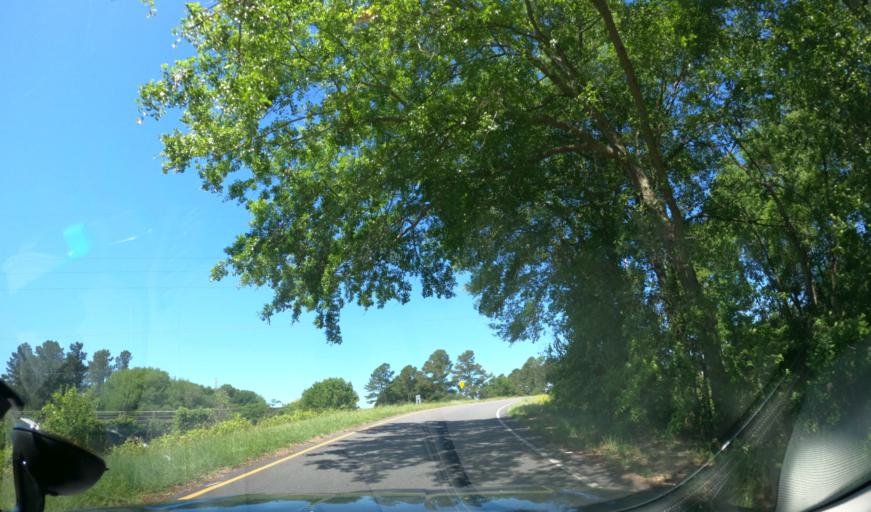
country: US
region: South Carolina
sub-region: Aiken County
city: Clearwater
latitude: 33.4894
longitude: -81.9195
